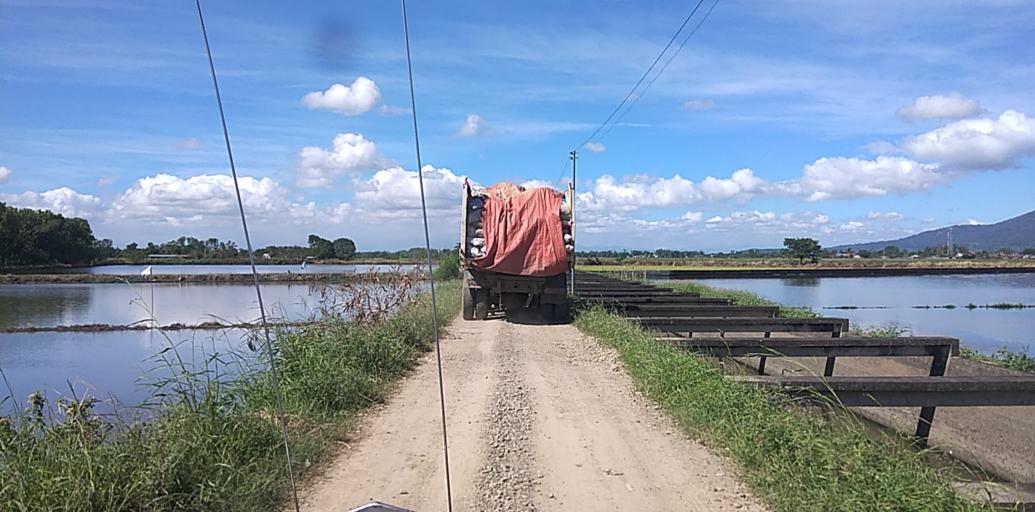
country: PH
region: Central Luzon
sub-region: Province of Pampanga
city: Candating
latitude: 15.1300
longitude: 120.8070
